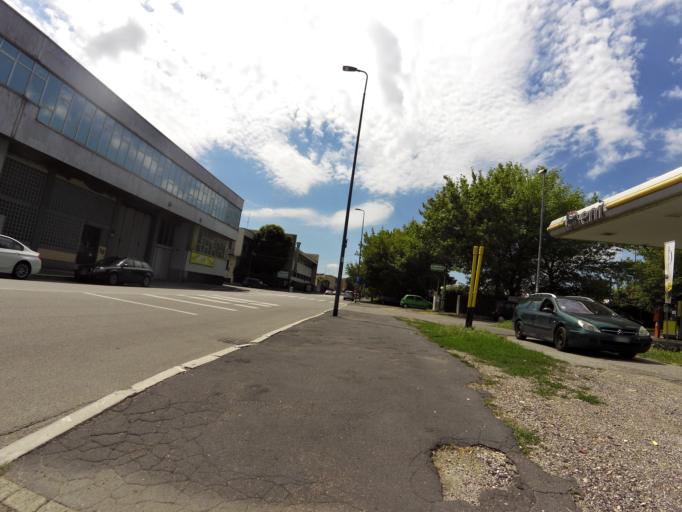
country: IT
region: Lombardy
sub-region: Citta metropolitana di Milano
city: Linate
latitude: 45.4515
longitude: 9.2414
